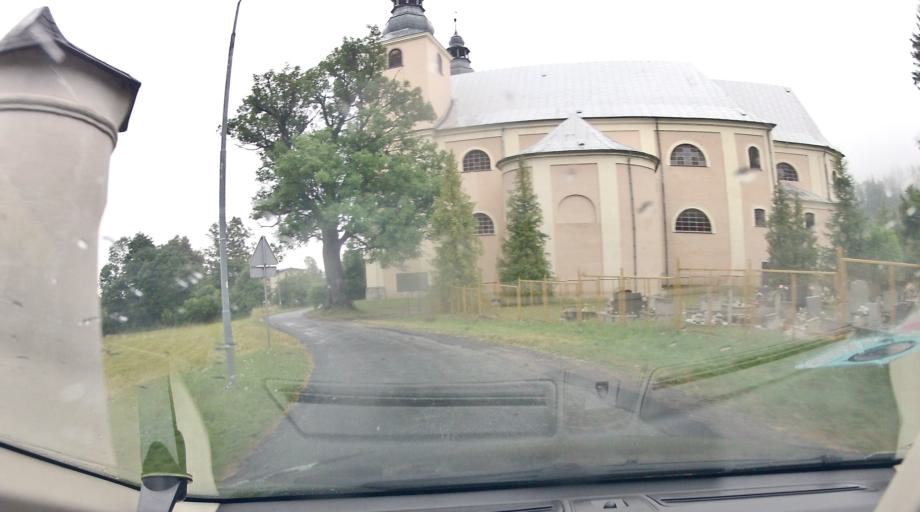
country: PL
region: Lower Silesian Voivodeship
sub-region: Powiat klodzki
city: Miedzylesie
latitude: 50.1978
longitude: 16.7457
